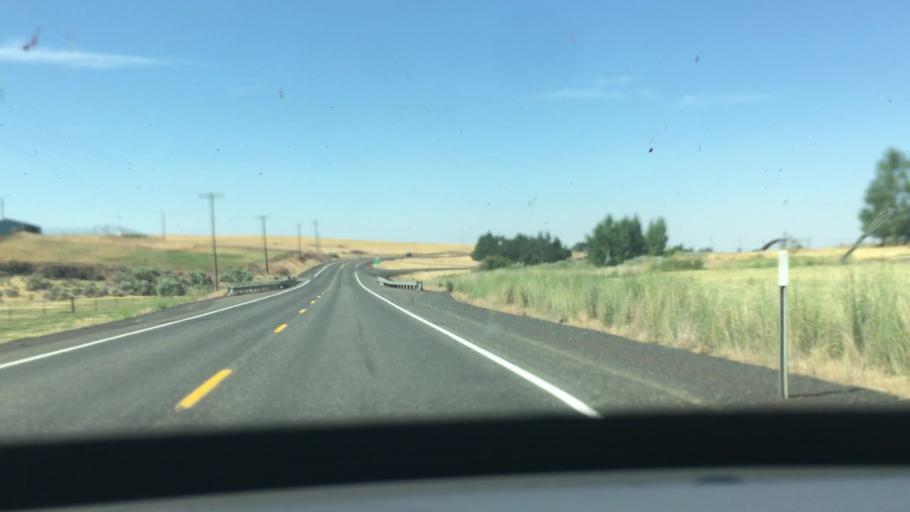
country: US
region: Oregon
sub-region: Sherman County
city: Moro
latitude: 45.4687
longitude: -120.7464
